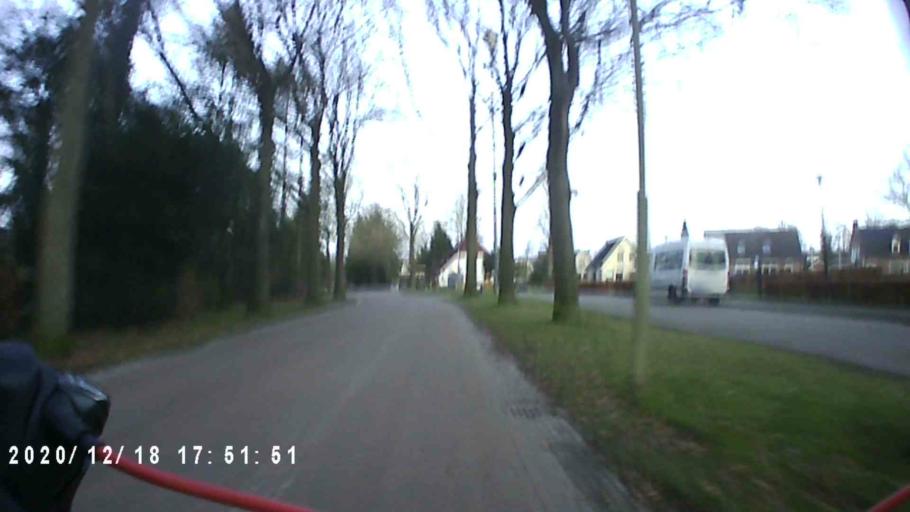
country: NL
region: Drenthe
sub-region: Gemeente Tynaarlo
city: Vries
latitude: 53.1171
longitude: 6.5929
